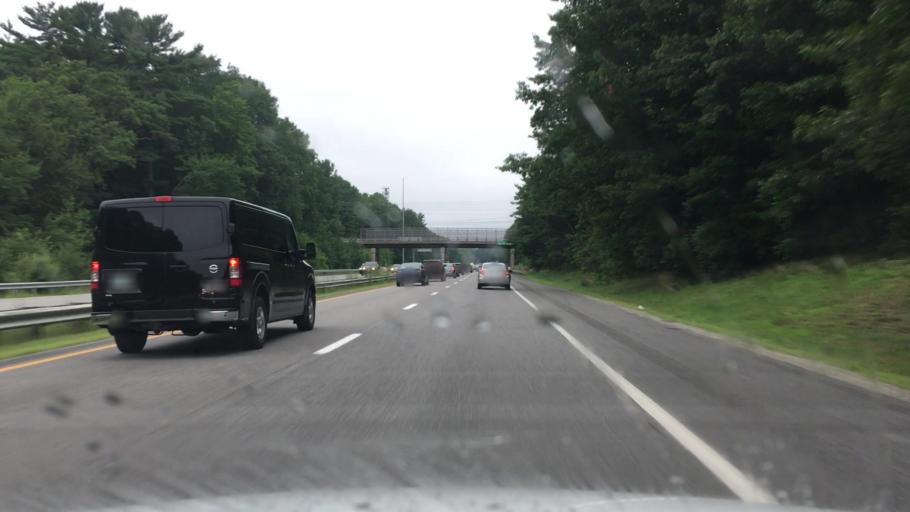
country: US
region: New Hampshire
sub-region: Strafford County
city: Dover
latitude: 43.1631
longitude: -70.8538
